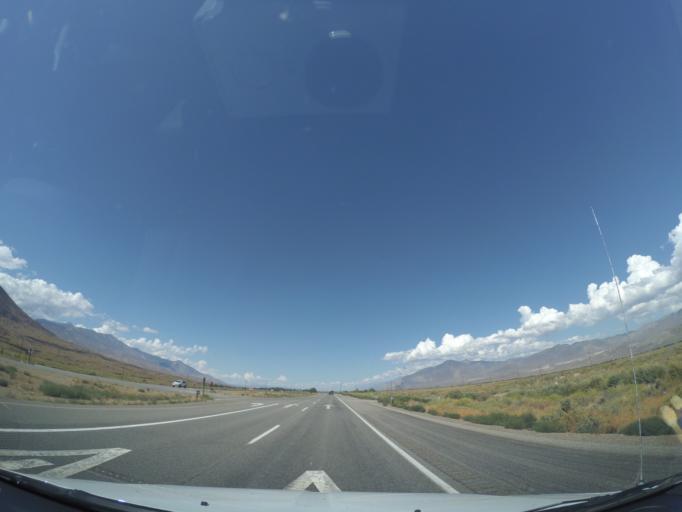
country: US
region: California
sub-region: Inyo County
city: Big Pine
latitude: 37.1053
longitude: -118.2526
